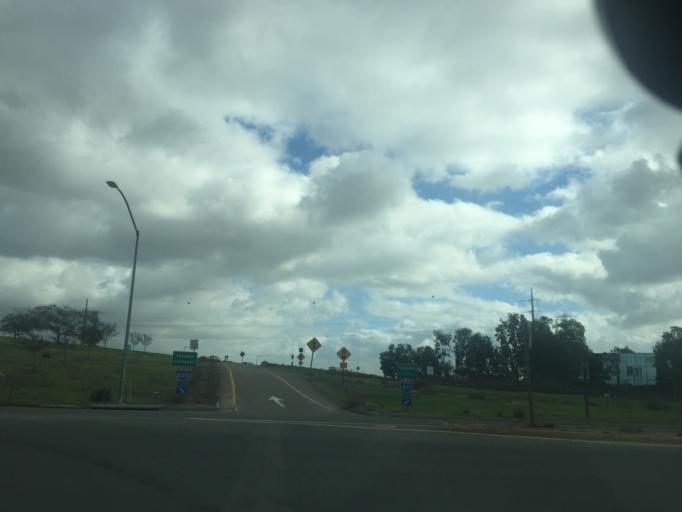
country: US
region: California
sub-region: San Diego County
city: La Jolla
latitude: 32.8572
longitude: -117.1853
